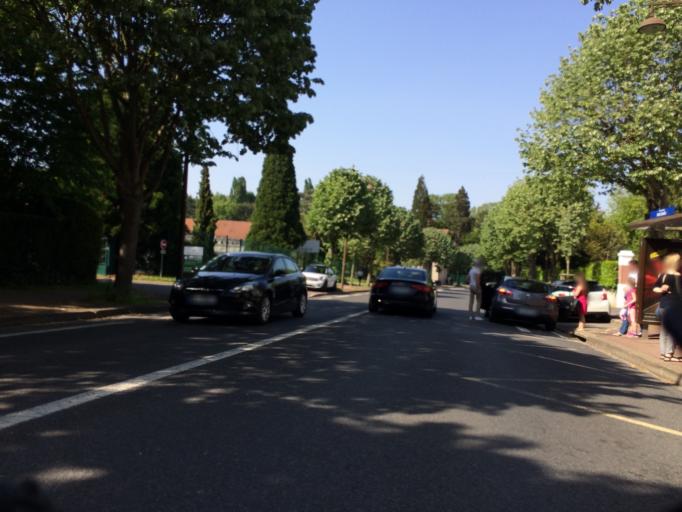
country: FR
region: Ile-de-France
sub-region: Departement des Hauts-de-Seine
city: Chatenay-Malabry
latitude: 48.7705
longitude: 2.2744
